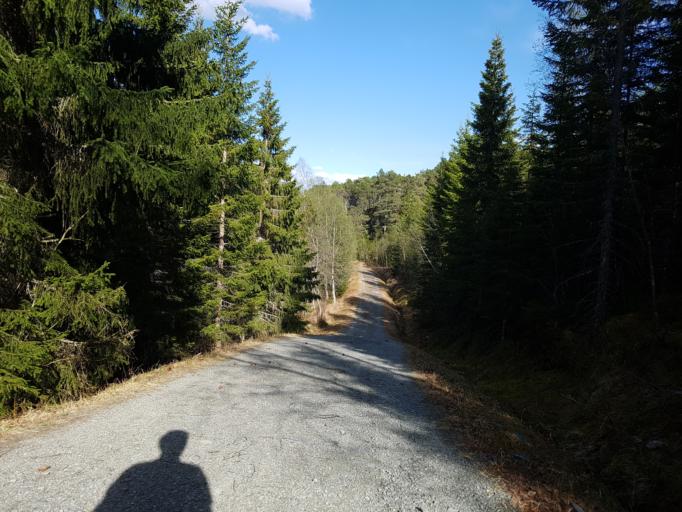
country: NO
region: Sor-Trondelag
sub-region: Trondheim
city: Trondheim
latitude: 63.4409
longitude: 10.3113
